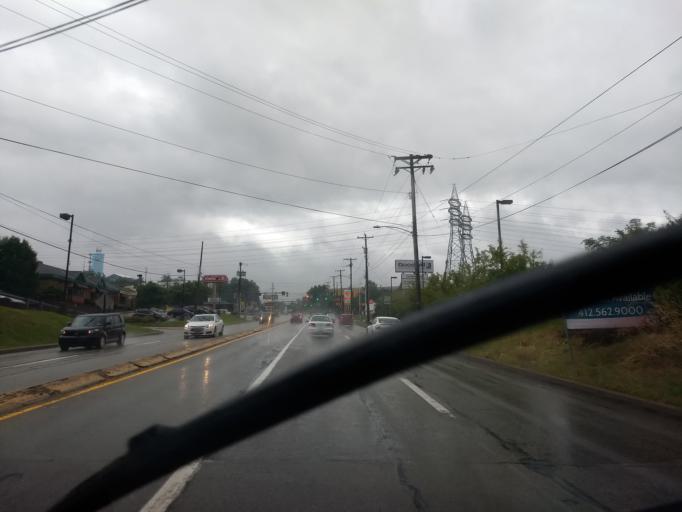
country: US
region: Pennsylvania
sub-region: Allegheny County
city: Wilmerding
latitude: 40.3855
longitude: -79.8255
